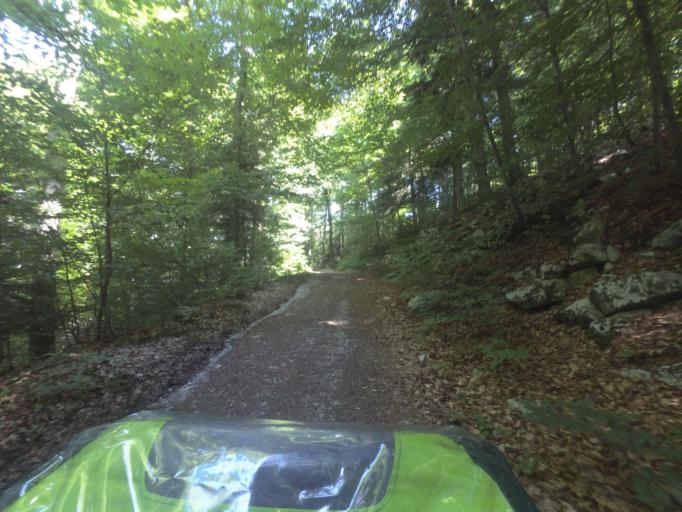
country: AT
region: Salzburg
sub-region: Politischer Bezirk Hallein
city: Oberalm
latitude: 47.7128
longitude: 13.1091
